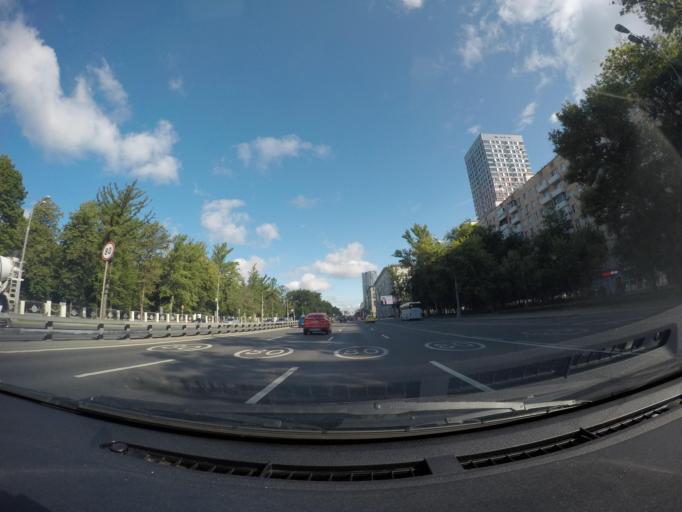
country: RU
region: Moskovskaya
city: Levoberezhnyy
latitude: 55.8542
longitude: 37.4711
